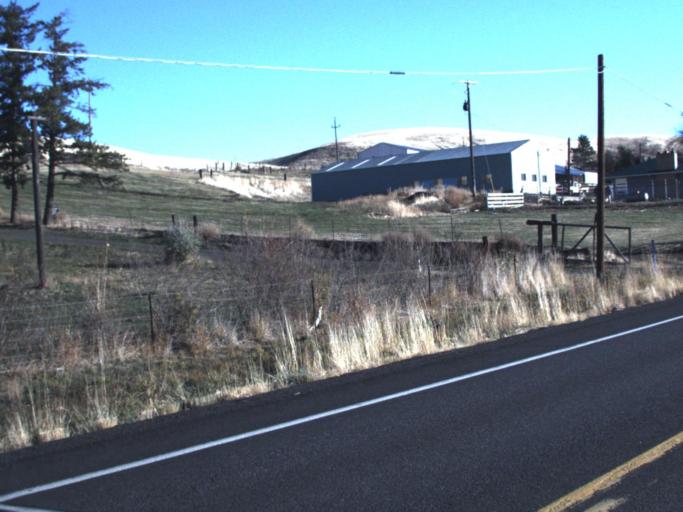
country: US
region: Washington
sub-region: Garfield County
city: Pomeroy
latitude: 46.4737
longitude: -117.5403
